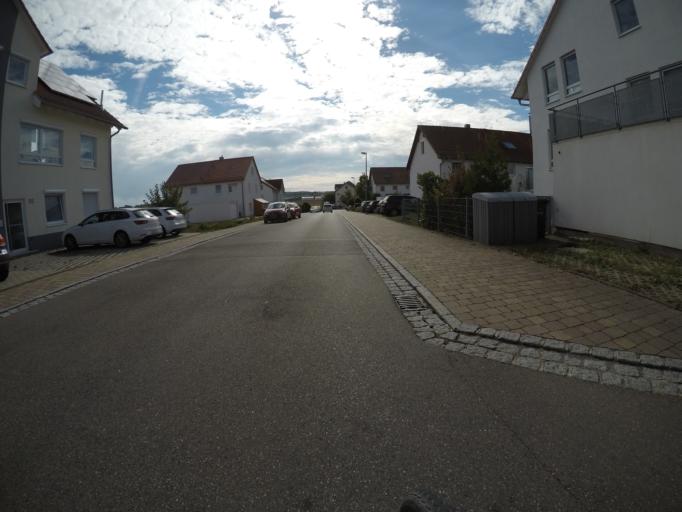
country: DE
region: Baden-Wuerttemberg
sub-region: Regierungsbezirk Stuttgart
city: Altdorf
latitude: 48.6330
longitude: 9.0024
